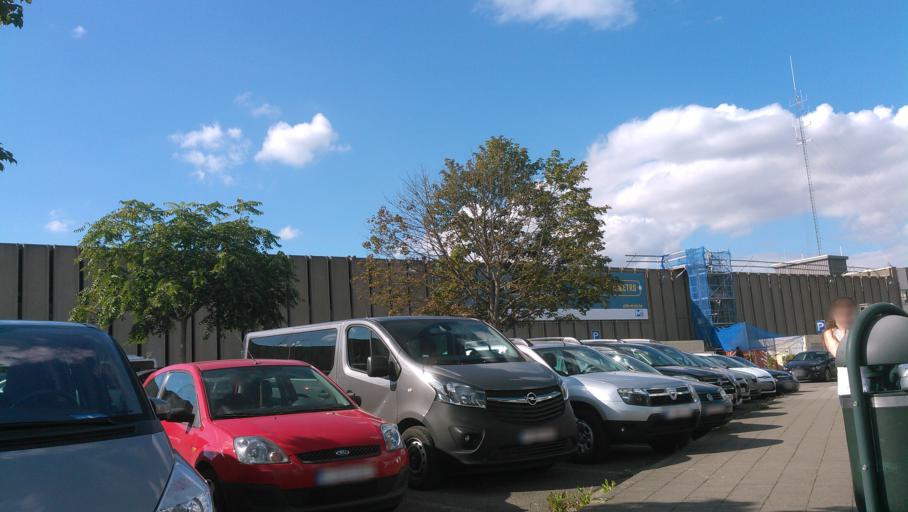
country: BE
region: Brussels Capital
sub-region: Bruxelles-Capitale
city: Brussels
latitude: 50.8357
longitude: 4.3648
